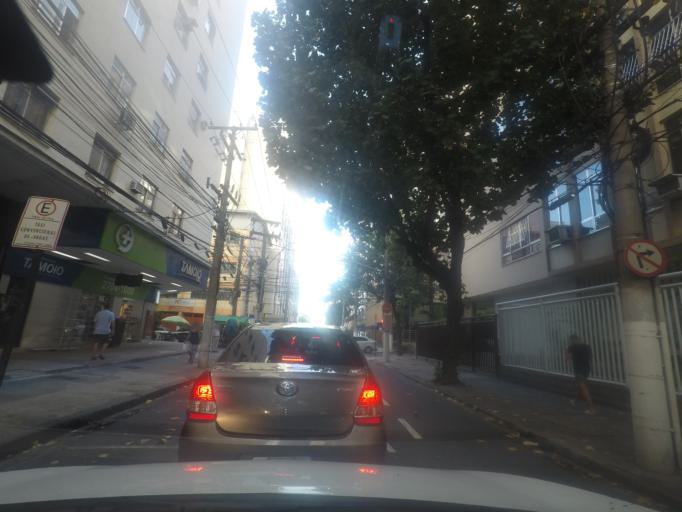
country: BR
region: Rio de Janeiro
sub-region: Niteroi
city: Niteroi
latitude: -22.9041
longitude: -43.1127
